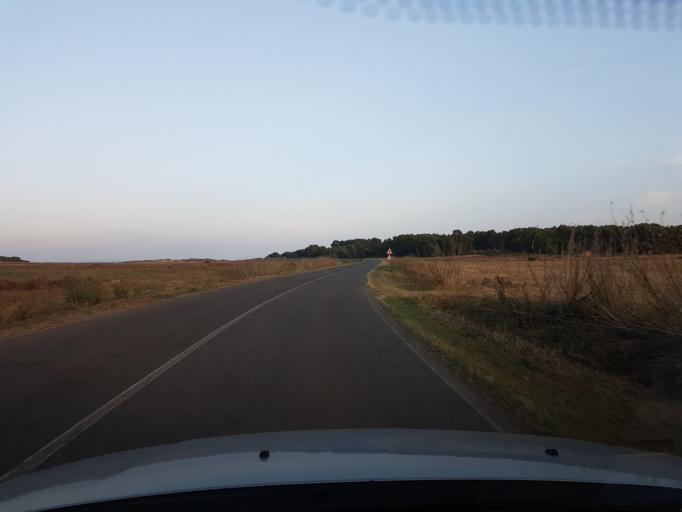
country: IT
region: Sardinia
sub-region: Provincia di Oristano
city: Cabras
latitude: 39.9396
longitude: 8.4410
